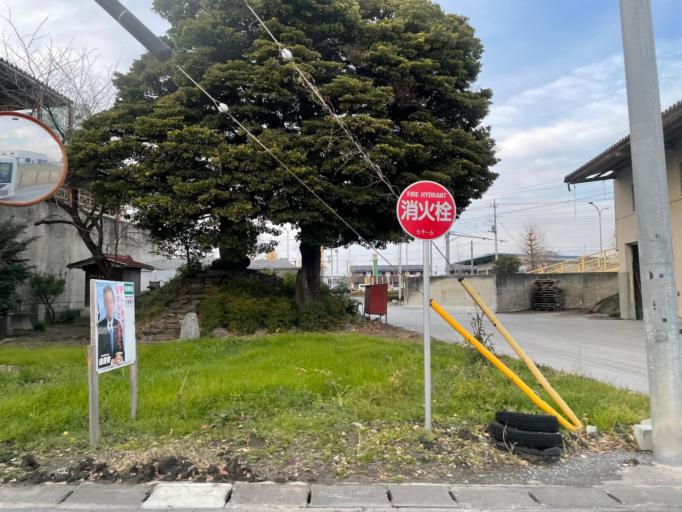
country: JP
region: Saitama
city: Yorii
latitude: 36.1223
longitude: 139.2069
